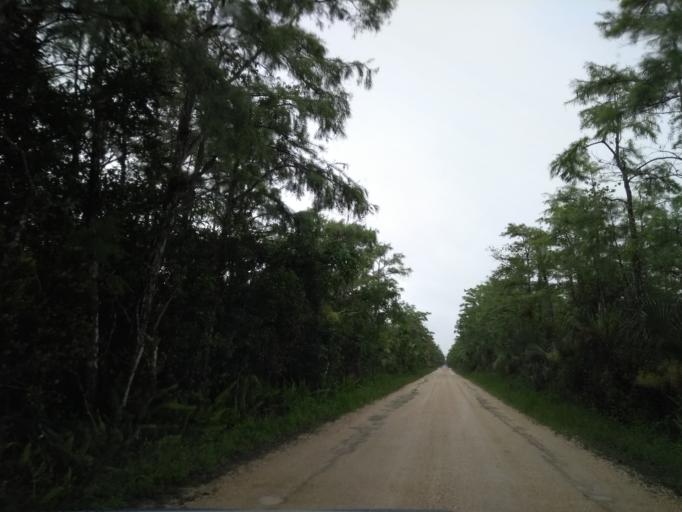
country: US
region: Florida
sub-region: Miami-Dade County
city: The Hammocks
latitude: 25.7602
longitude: -81.0415
